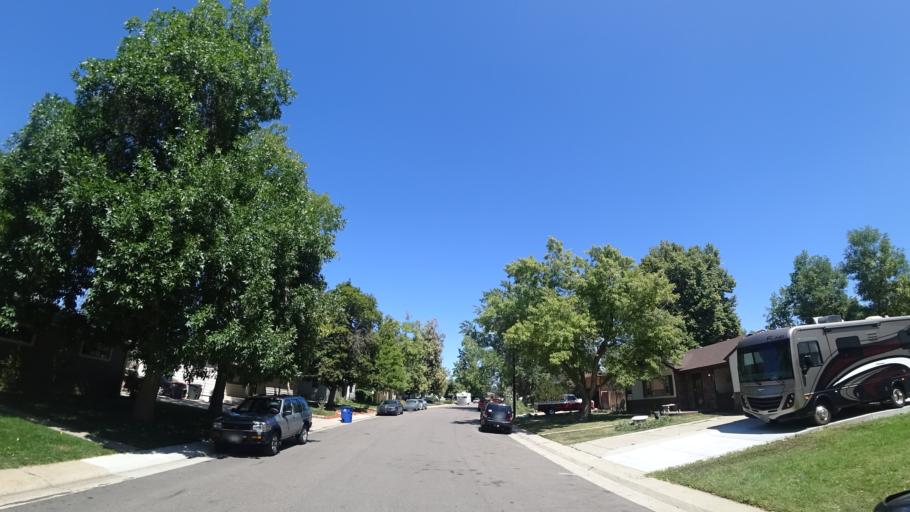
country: US
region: Colorado
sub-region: Arapahoe County
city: Littleton
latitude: 39.6112
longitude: -104.9981
